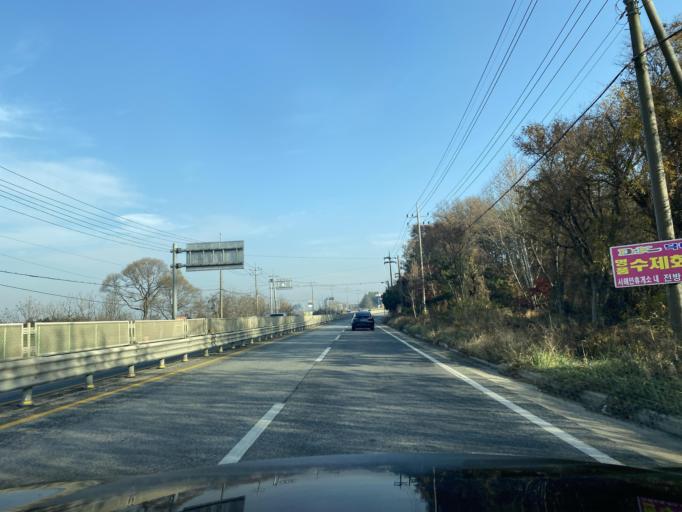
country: KR
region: Chungcheongnam-do
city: Yesan
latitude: 36.7423
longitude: 126.8603
